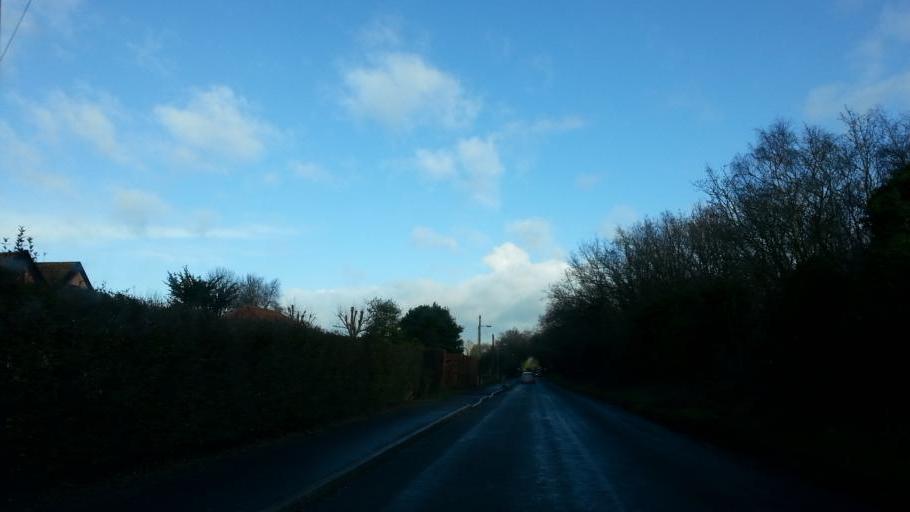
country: GB
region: England
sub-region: Norfolk
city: Ditchingham
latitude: 52.4701
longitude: 1.4490
